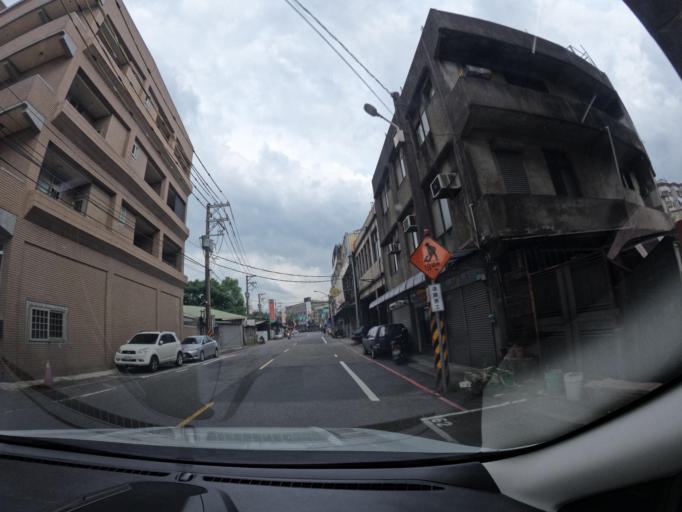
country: TW
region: Taiwan
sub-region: Taoyuan
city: Taoyuan
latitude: 24.9523
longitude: 121.3418
